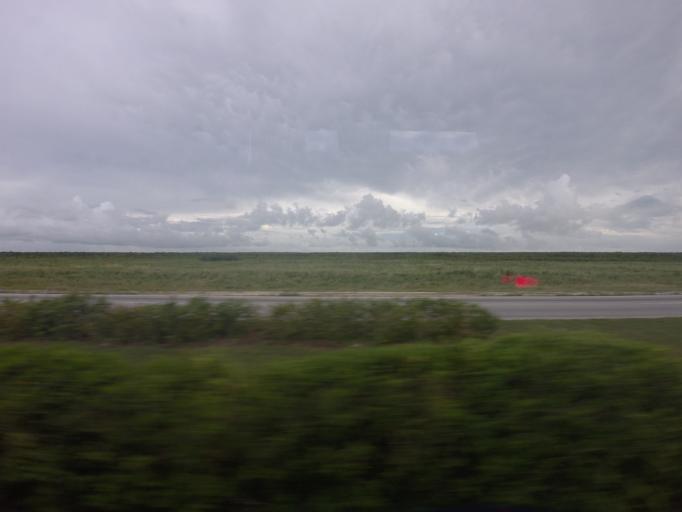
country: CU
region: Matanzas
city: Varadero
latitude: 23.0982
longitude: -81.4091
